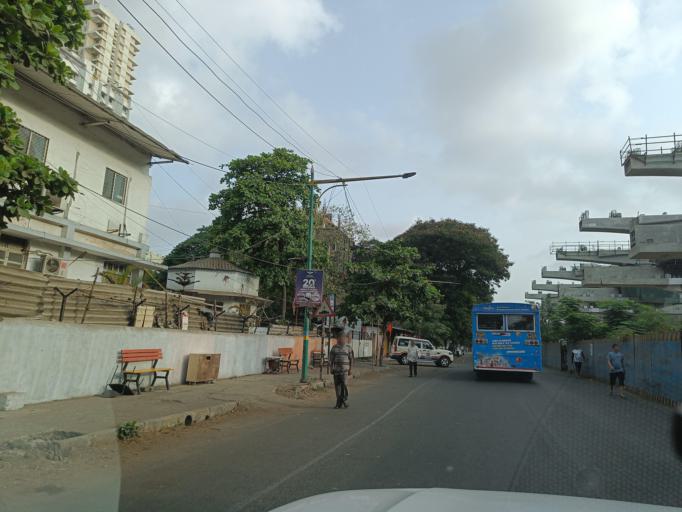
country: IN
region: Maharashtra
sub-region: Thane
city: Thane
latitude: 19.1923
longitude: 72.9626
